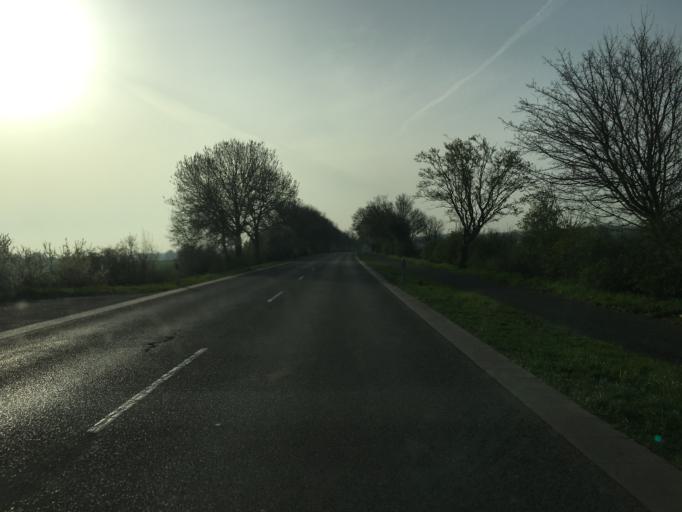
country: DE
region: North Rhine-Westphalia
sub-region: Regierungsbezirk Koln
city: Hurth
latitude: 50.8952
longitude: 6.8488
